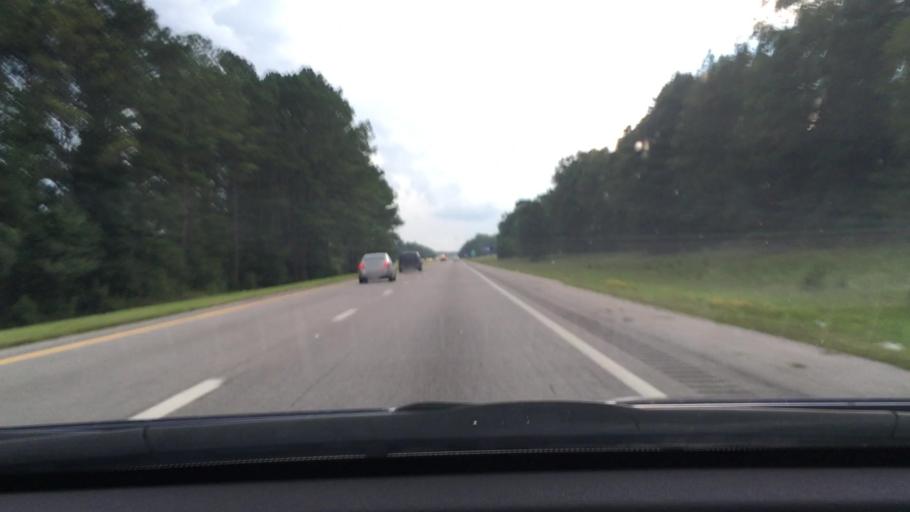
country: US
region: South Carolina
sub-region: Kershaw County
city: Camden
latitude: 34.2140
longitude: -80.5644
